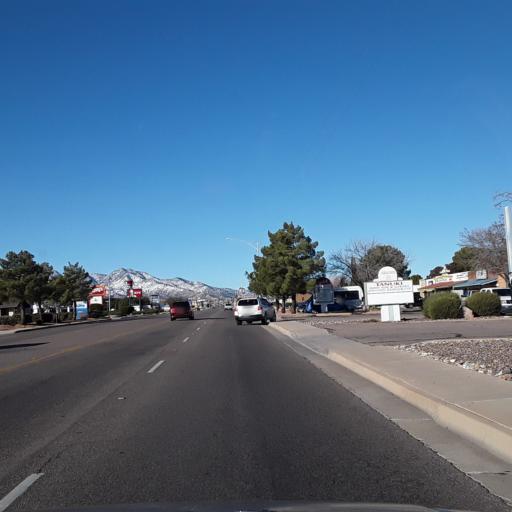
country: US
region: Arizona
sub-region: Cochise County
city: Sierra Vista
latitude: 31.5547
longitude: -110.2853
